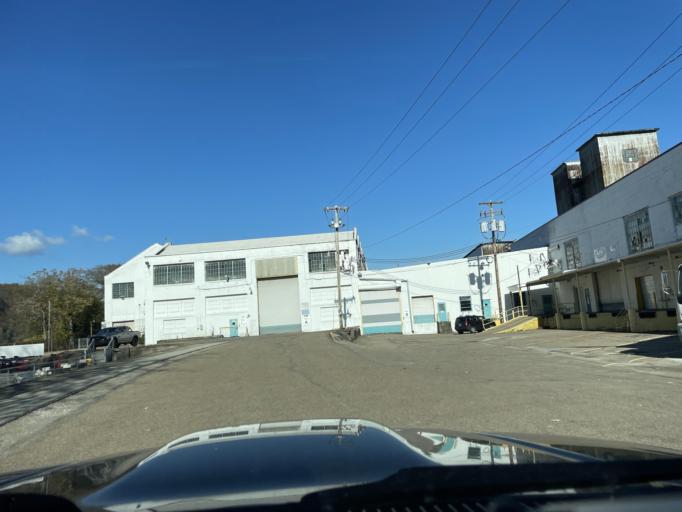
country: US
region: Pennsylvania
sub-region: Westmoreland County
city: New Kensington
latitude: 40.5713
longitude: -79.7715
